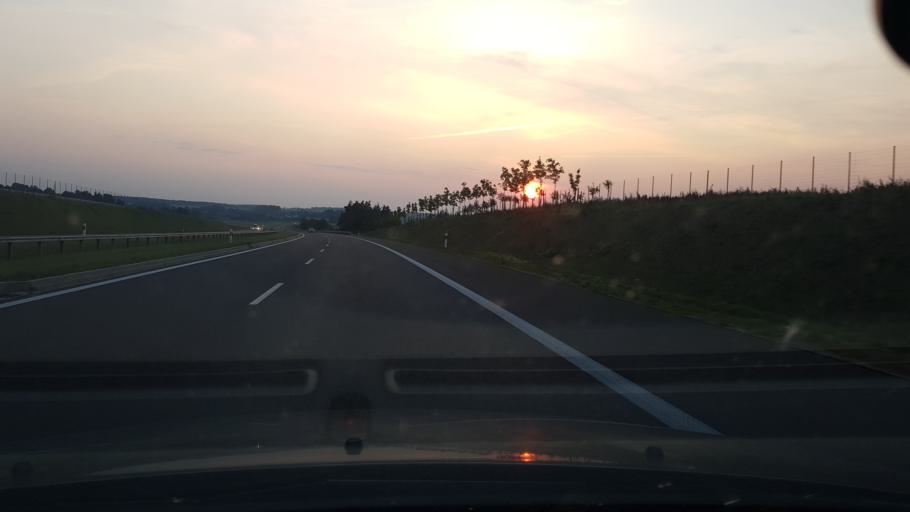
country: PL
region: Warmian-Masurian Voivodeship
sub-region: Powiat nidzicki
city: Nidzica
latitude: 53.3391
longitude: 20.4242
